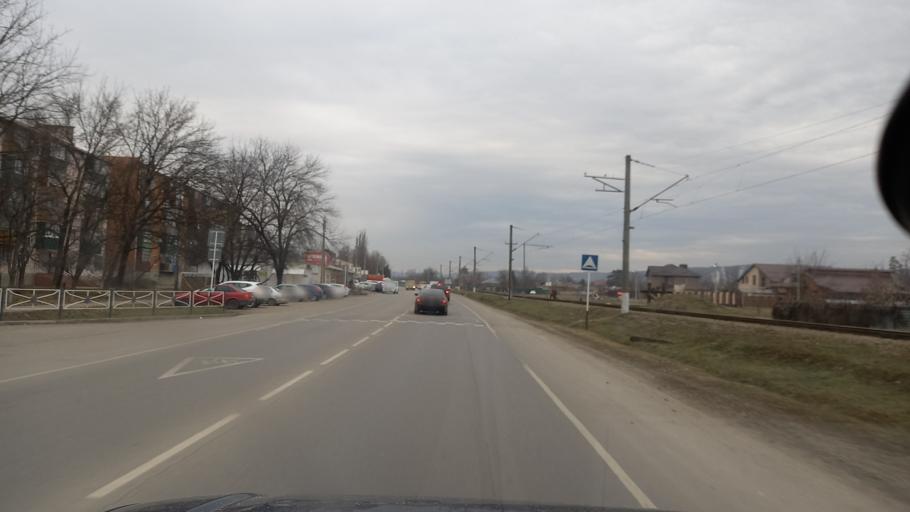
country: RU
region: Adygeya
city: Maykop
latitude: 44.5954
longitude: 40.1320
